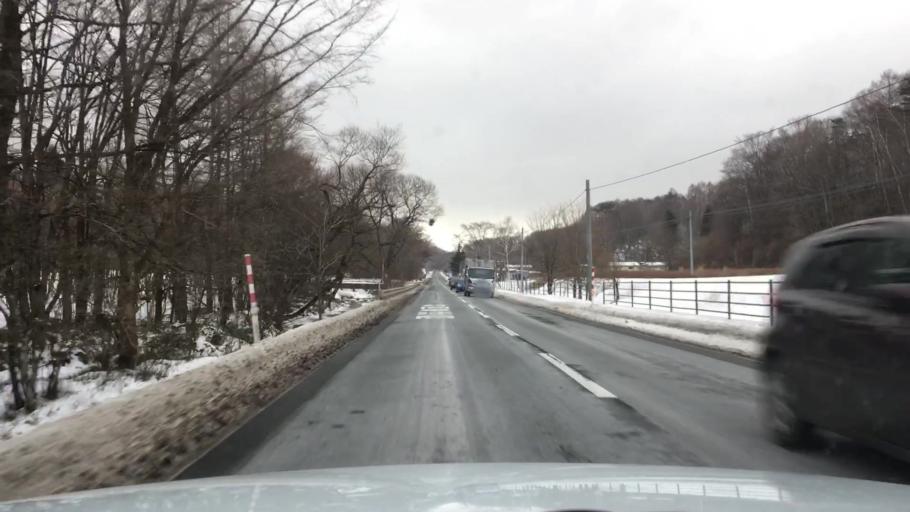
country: JP
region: Iwate
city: Morioka-shi
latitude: 39.6414
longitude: 141.4190
